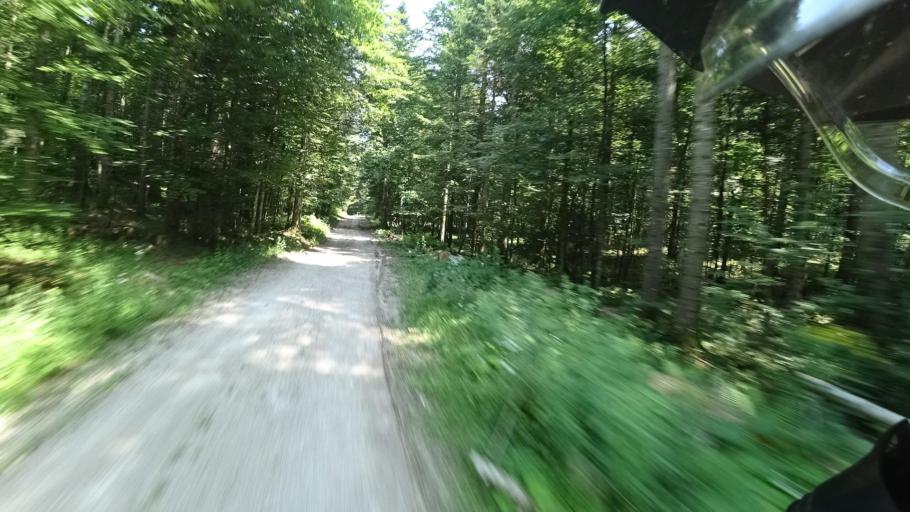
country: HR
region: Primorsko-Goranska
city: Vrbovsko
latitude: 45.3432
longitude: 15.0394
